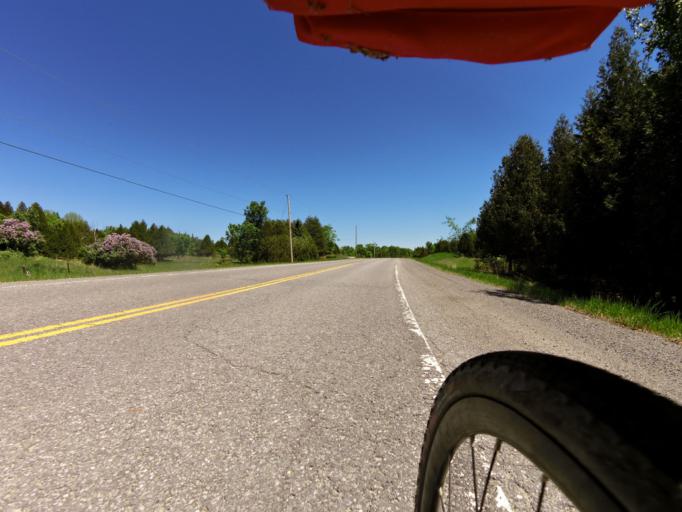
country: CA
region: Ontario
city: Carleton Place
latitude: 45.1840
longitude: -76.3804
